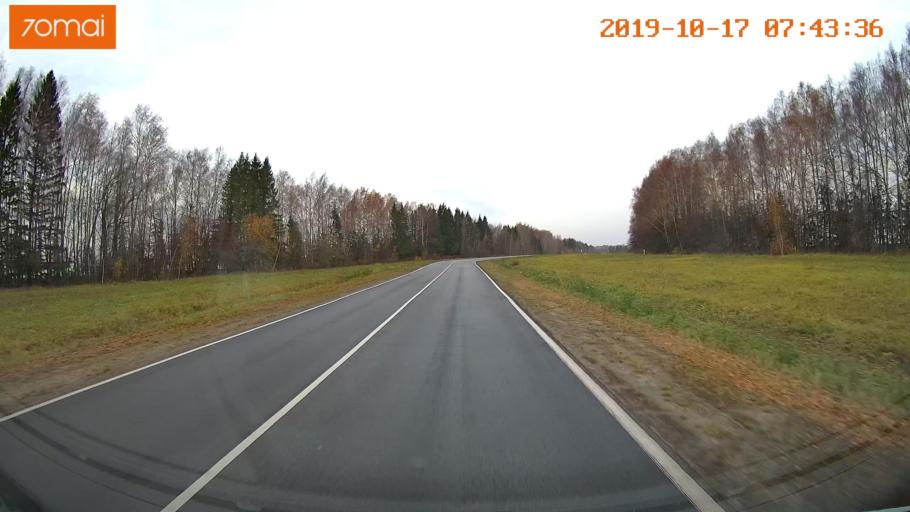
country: RU
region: Vladimir
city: Yur'yev-Pol'skiy
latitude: 56.4832
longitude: 39.7608
